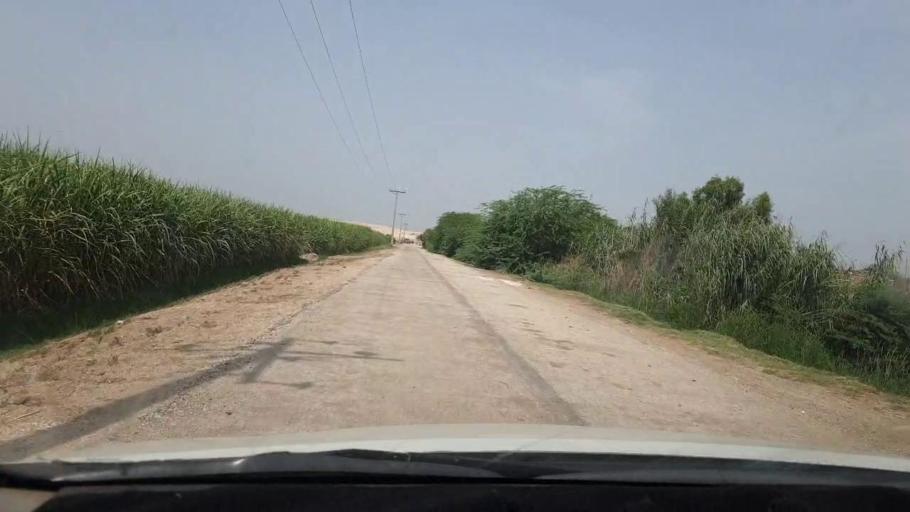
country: PK
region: Sindh
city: Rohri
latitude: 27.5957
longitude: 68.9814
